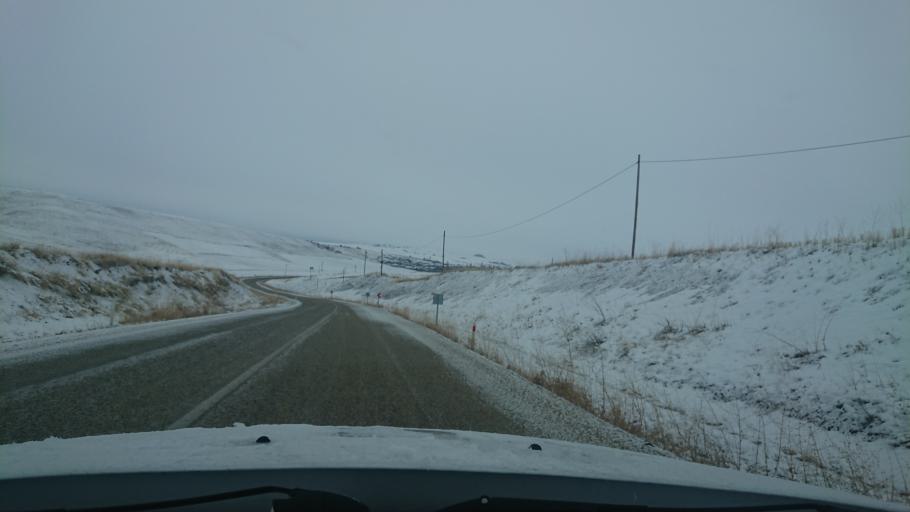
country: TR
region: Aksaray
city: Agacoren
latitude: 38.7940
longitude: 33.8707
